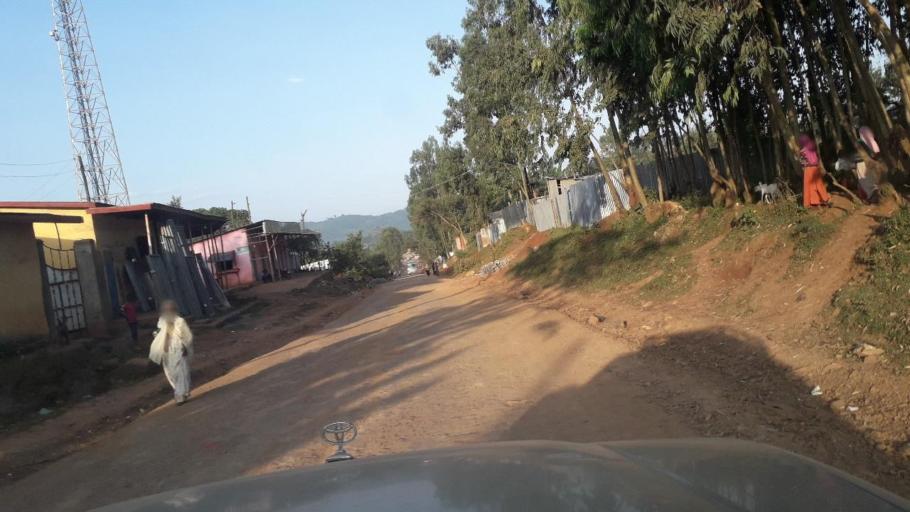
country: ET
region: Oromiya
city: Jima
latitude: 7.6383
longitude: 36.8380
